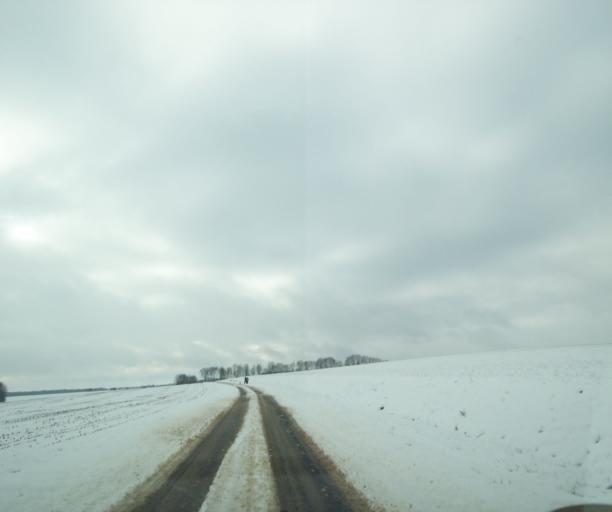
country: FR
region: Champagne-Ardenne
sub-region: Departement de la Haute-Marne
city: Montier-en-Der
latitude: 48.5069
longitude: 4.6875
